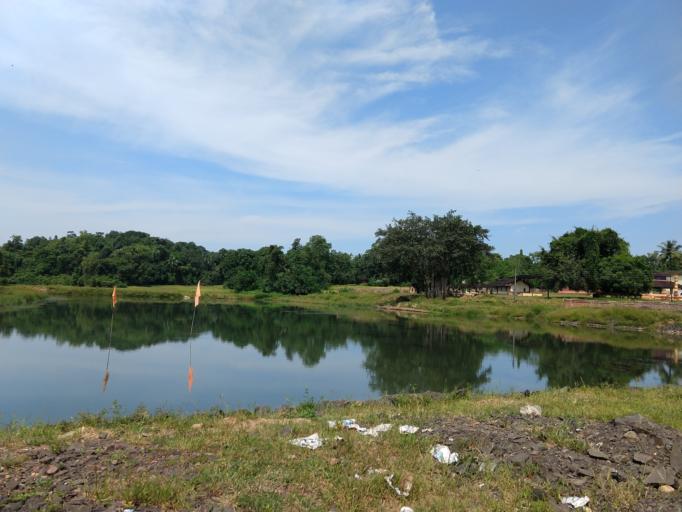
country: IN
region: Maharashtra
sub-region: Sindhudurg
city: Kudal
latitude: 16.0434
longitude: 73.6843
